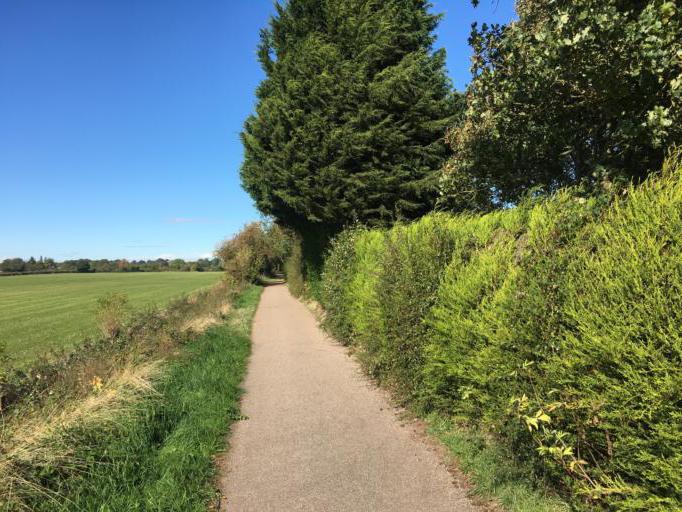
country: GB
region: England
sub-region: Warwickshire
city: Kenilworth
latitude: 52.3682
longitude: -1.5849
